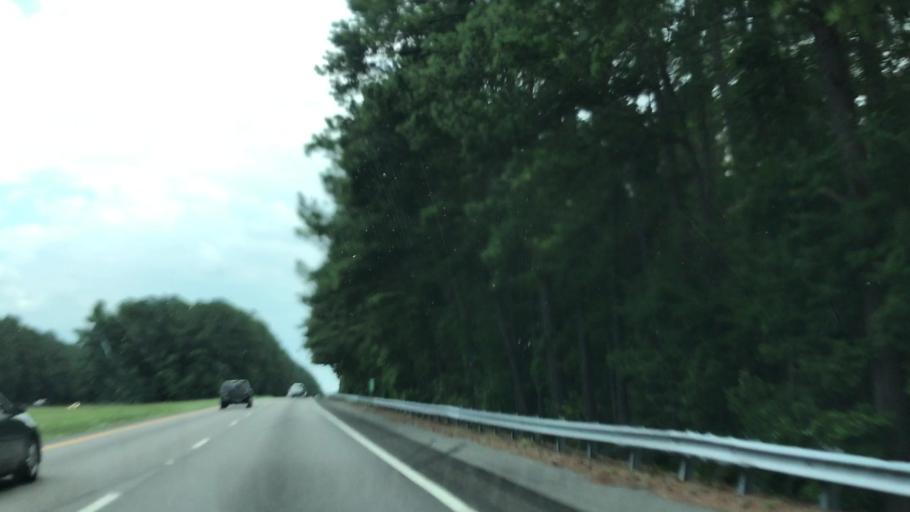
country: US
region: South Carolina
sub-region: Richland County
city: Blythewood
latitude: 34.2644
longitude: -80.9982
